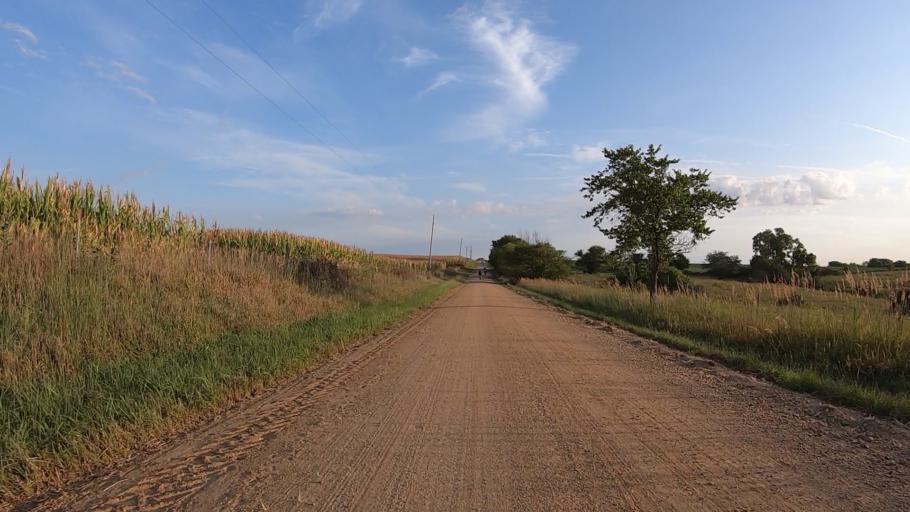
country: US
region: Kansas
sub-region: Marshall County
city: Marysville
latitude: 39.7663
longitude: -96.7130
